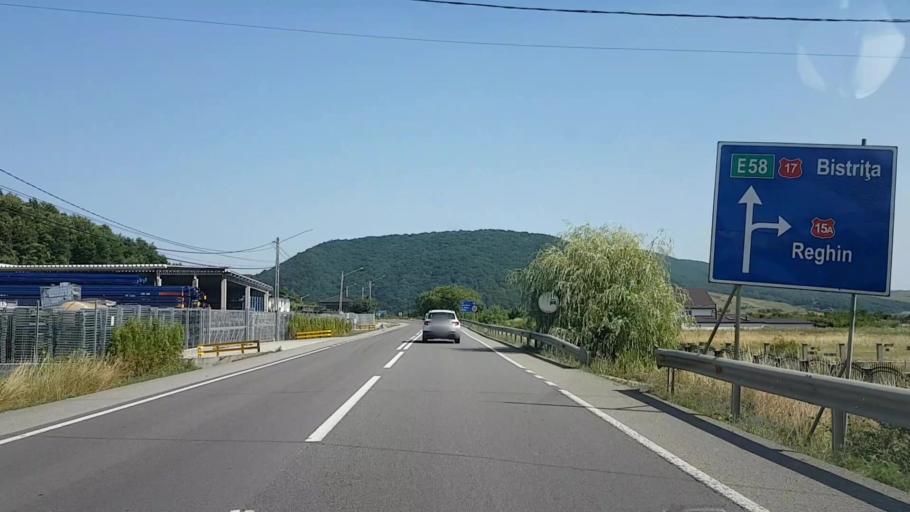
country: RO
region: Bistrita-Nasaud
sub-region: Comuna Sieu-Magherus
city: Sieu-Magherus
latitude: 47.0655
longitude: 24.4128
